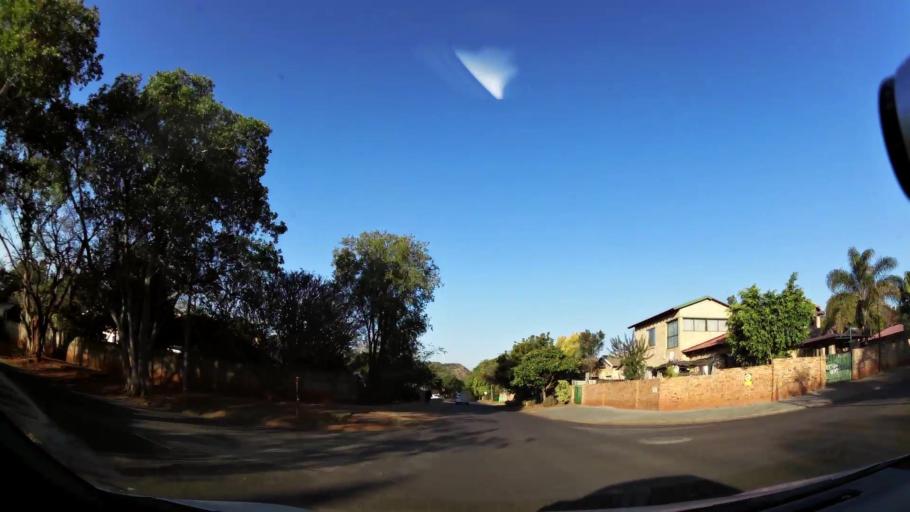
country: ZA
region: North-West
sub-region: Bojanala Platinum District Municipality
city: Rustenburg
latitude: -25.6935
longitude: 27.2145
